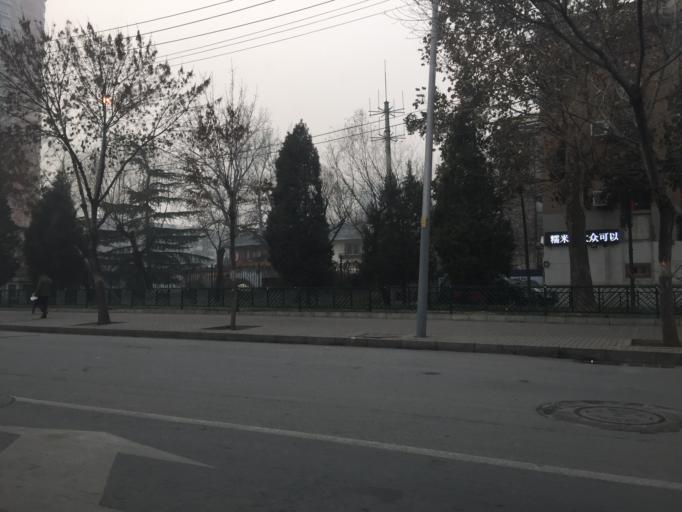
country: CN
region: Beijing
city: Qinghe
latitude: 40.0070
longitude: 116.3462
